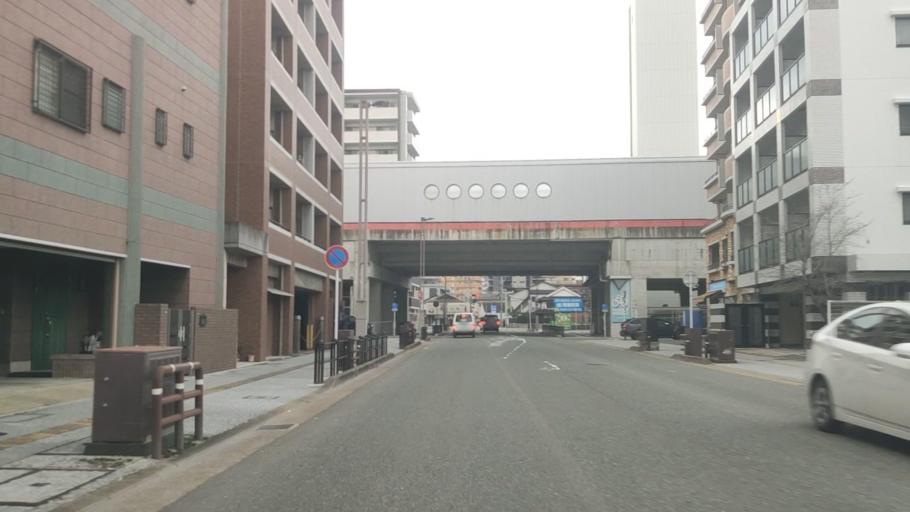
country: JP
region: Fukuoka
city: Fukuoka-shi
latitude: 33.6171
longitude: 130.4277
